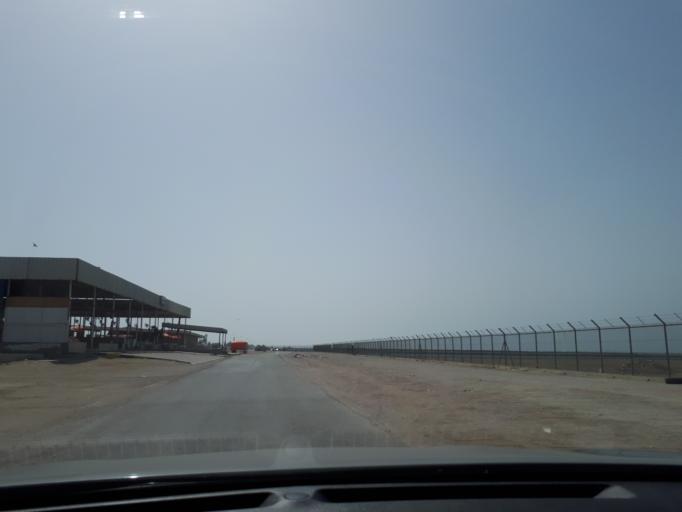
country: OM
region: Al Batinah
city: Barka'
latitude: 23.7096
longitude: 57.8966
